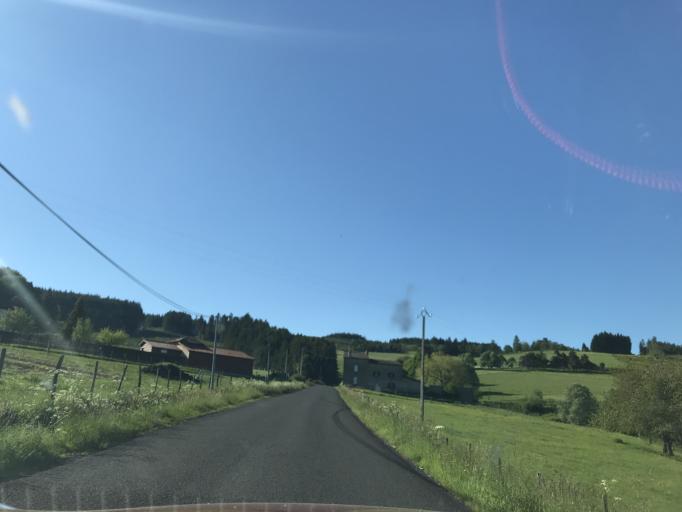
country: FR
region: Auvergne
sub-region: Departement du Puy-de-Dome
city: Cunlhat
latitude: 45.5815
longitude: 3.6389
